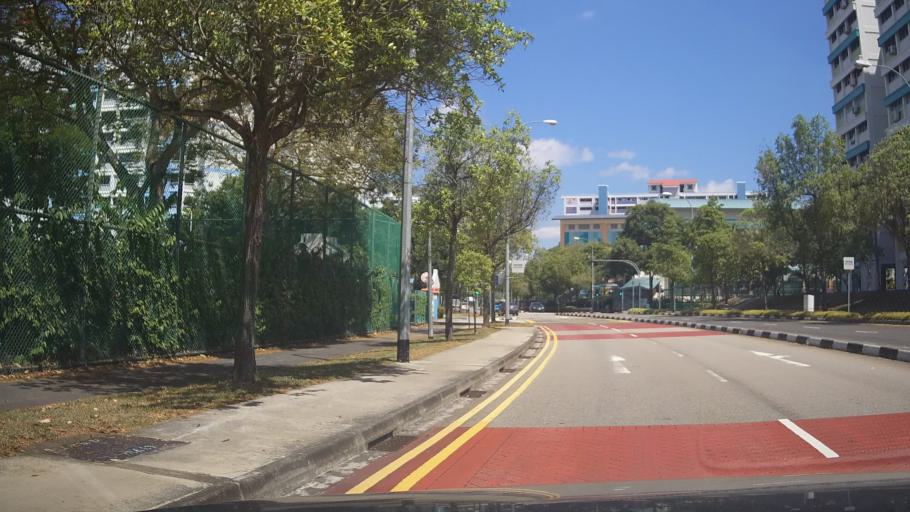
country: MY
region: Johor
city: Kampung Pasir Gudang Baru
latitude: 1.3711
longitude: 103.9569
